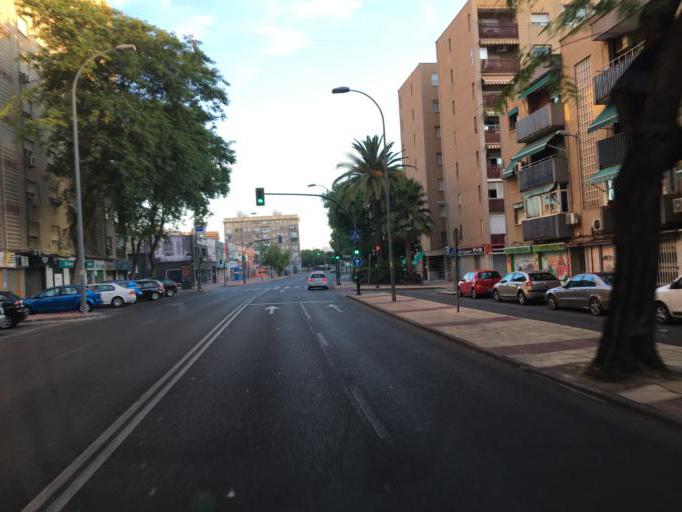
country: ES
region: Murcia
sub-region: Murcia
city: Murcia
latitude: 37.9955
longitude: -1.1425
